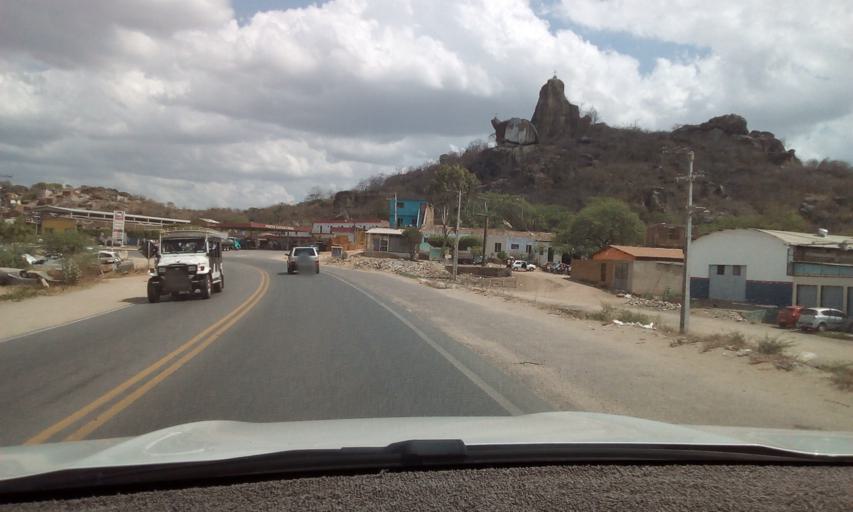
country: BR
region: Pernambuco
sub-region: Toritama
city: Toritama
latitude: -8.0128
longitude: -36.0571
